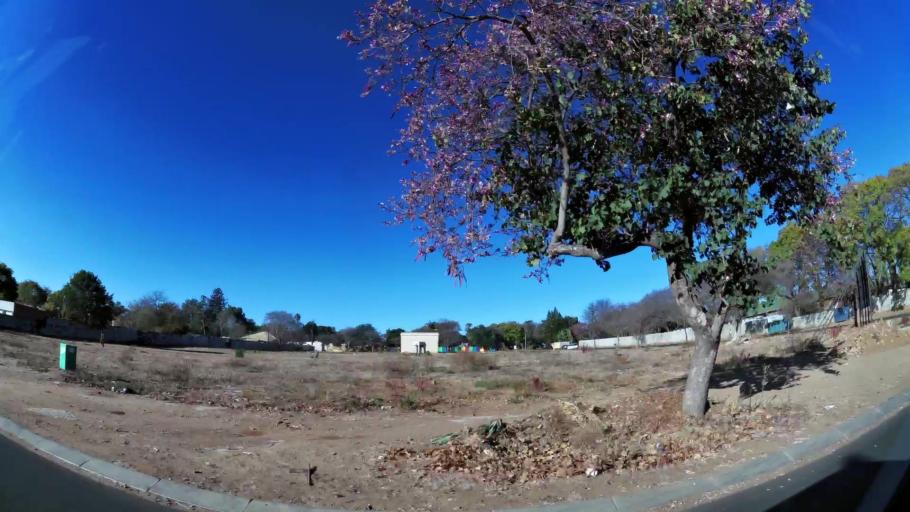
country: ZA
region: Limpopo
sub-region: Capricorn District Municipality
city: Polokwane
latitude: -23.9039
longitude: 29.4658
